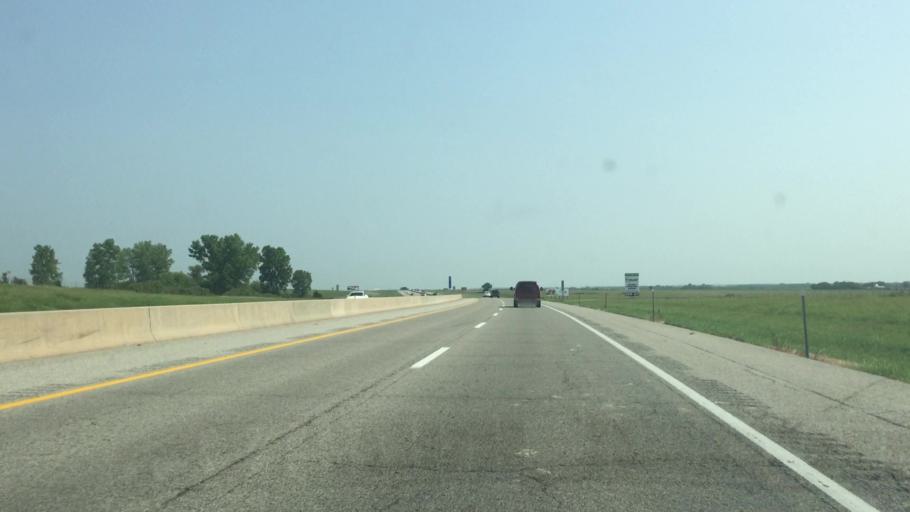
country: US
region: Kansas
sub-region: Lyon County
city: Emporia
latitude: 38.3411
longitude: -96.2951
